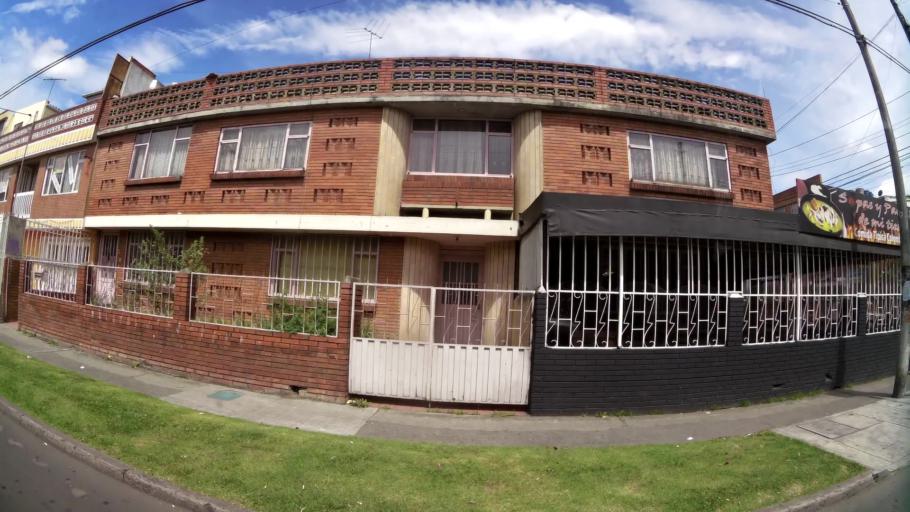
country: CO
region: Bogota D.C.
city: Bogota
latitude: 4.6275
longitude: -74.1335
